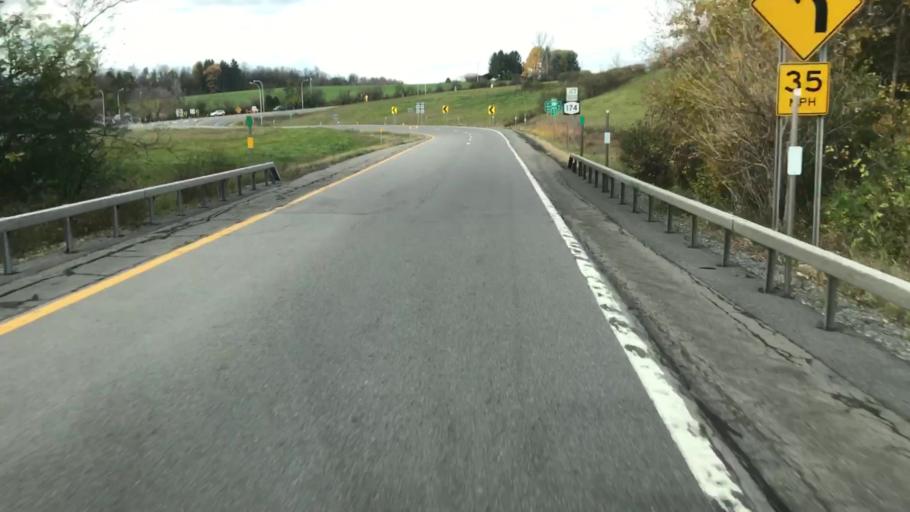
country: US
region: New York
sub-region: Onondaga County
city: Camillus
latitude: 43.0371
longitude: -76.3220
